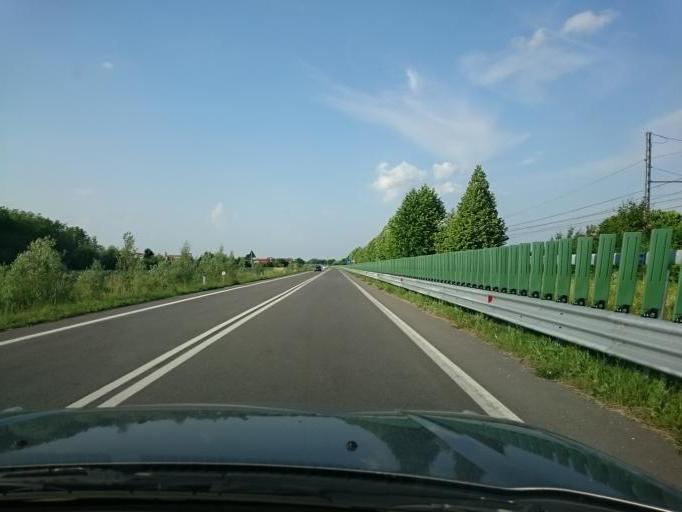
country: IT
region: Veneto
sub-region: Provincia di Padova
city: Tencarola
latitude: 45.3722
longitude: 11.8236
